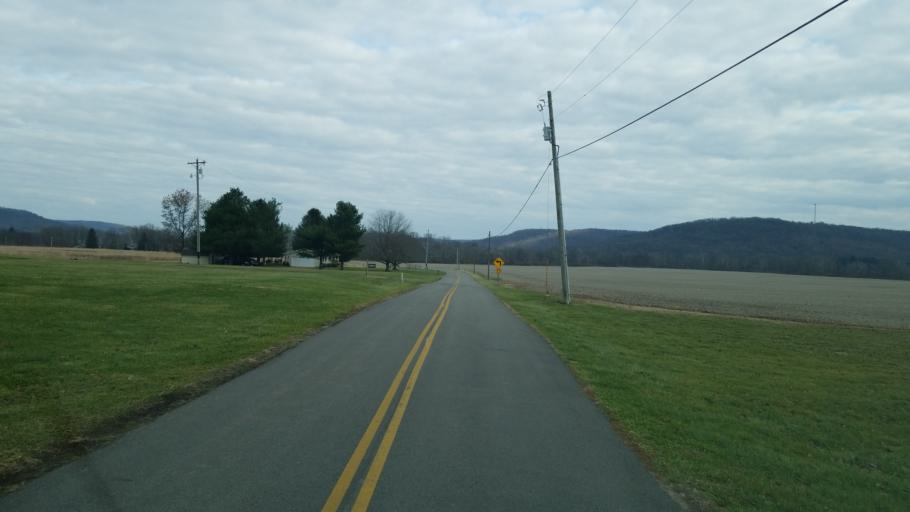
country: US
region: Ohio
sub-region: Highland County
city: Greenfield
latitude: 39.2268
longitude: -83.3030
